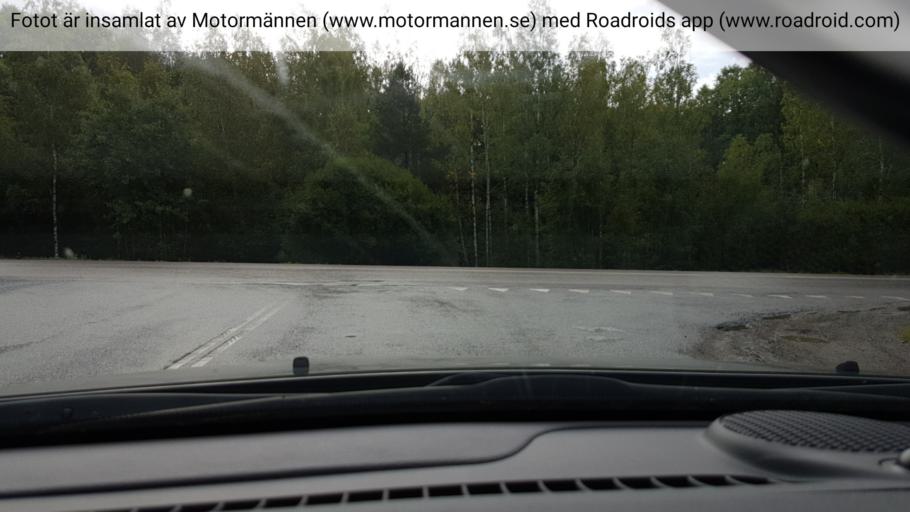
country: SE
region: Stockholm
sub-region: Haninge Kommun
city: Handen
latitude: 59.1964
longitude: 18.1204
